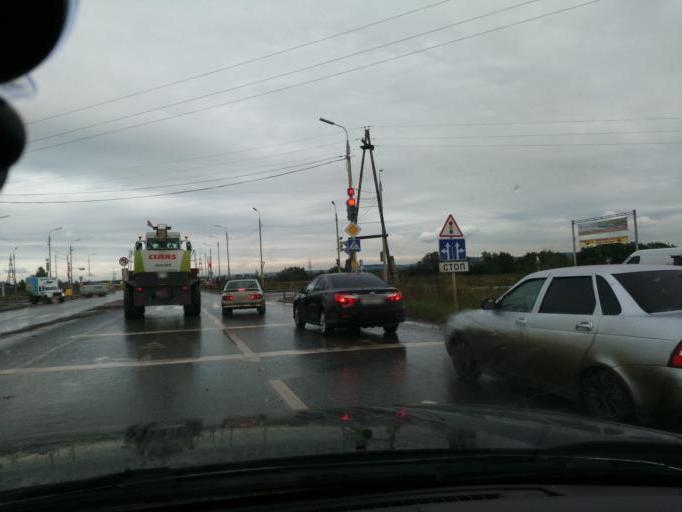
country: RU
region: Perm
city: Kultayevo
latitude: 57.8842
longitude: 55.9224
